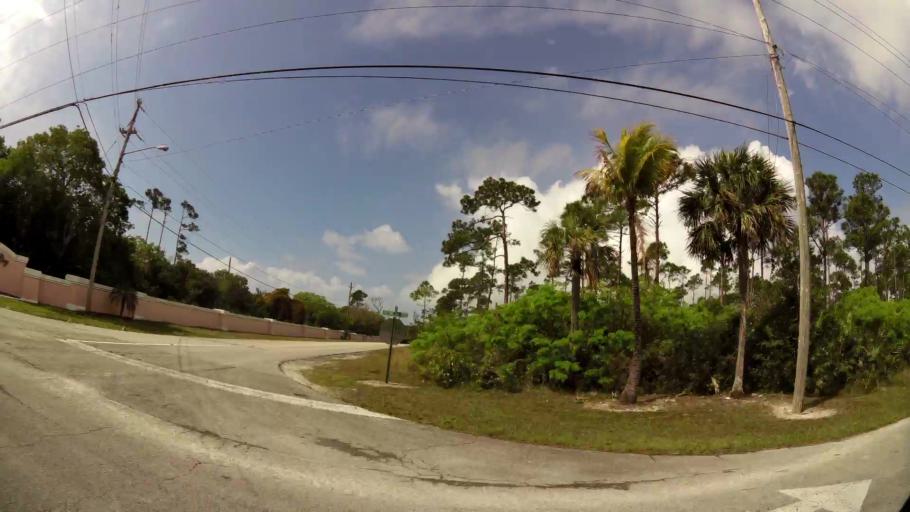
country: BS
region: Freeport
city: Lucaya
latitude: 26.5445
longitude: -78.5823
